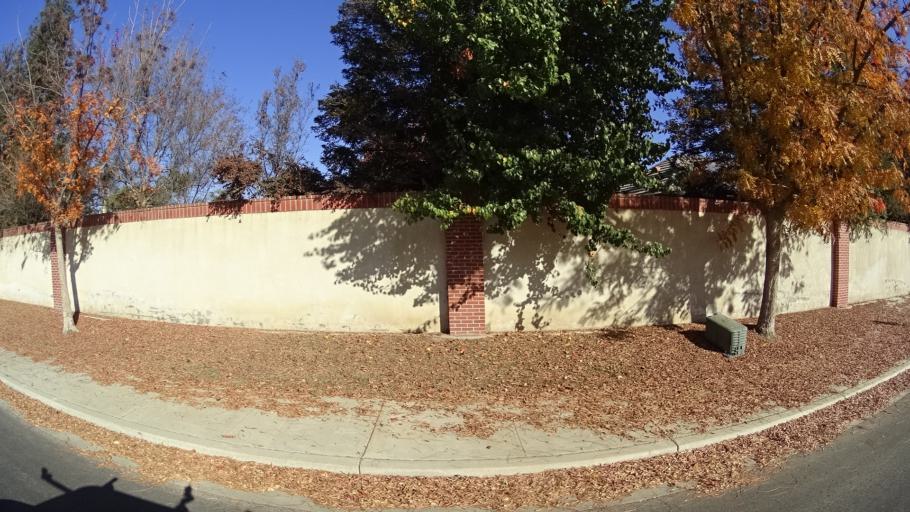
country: US
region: California
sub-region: Kern County
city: Rosedale
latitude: 35.3288
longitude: -119.1416
